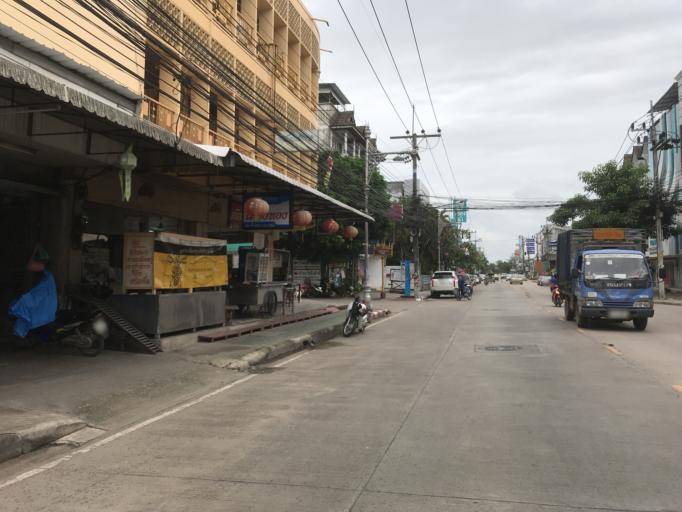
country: TH
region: Chiang Rai
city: Chiang Rai
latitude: 19.9037
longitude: 99.8330
